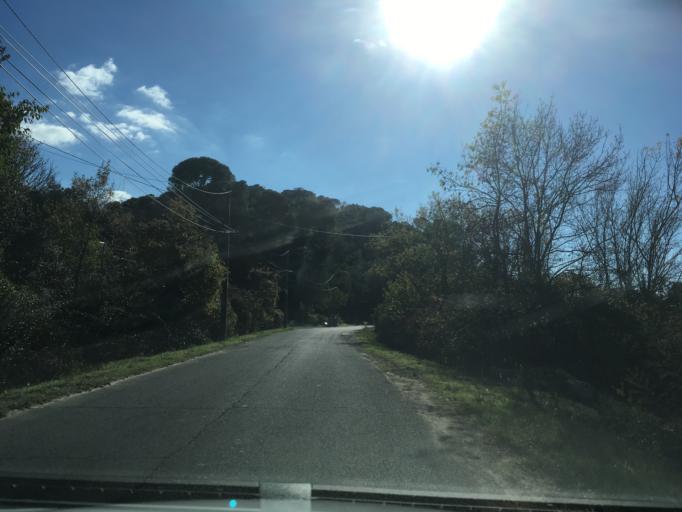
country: FR
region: Languedoc-Roussillon
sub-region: Departement de l'Herault
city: Juvignac
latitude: 43.6054
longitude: 3.8216
